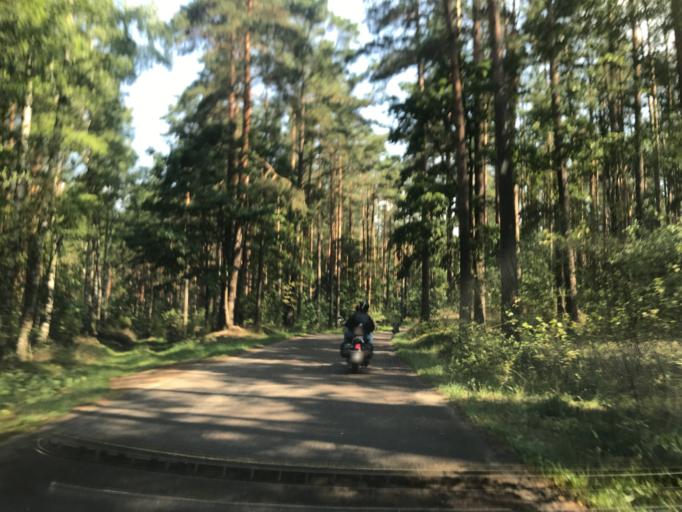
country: PL
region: Warmian-Masurian Voivodeship
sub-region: Powiat nowomiejski
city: Biskupiec
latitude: 53.4388
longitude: 19.4372
